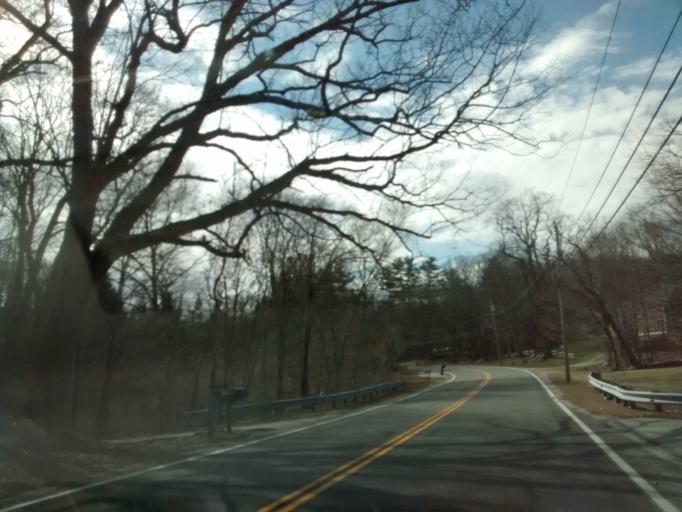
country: US
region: Rhode Island
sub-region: Providence County
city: Harrisville
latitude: 41.9831
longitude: -71.6959
